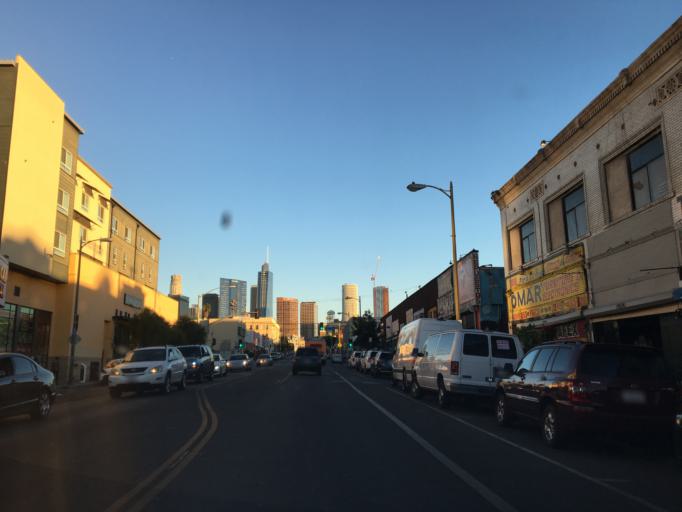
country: US
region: California
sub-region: Los Angeles County
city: Echo Park
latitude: 34.0558
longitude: -118.2755
